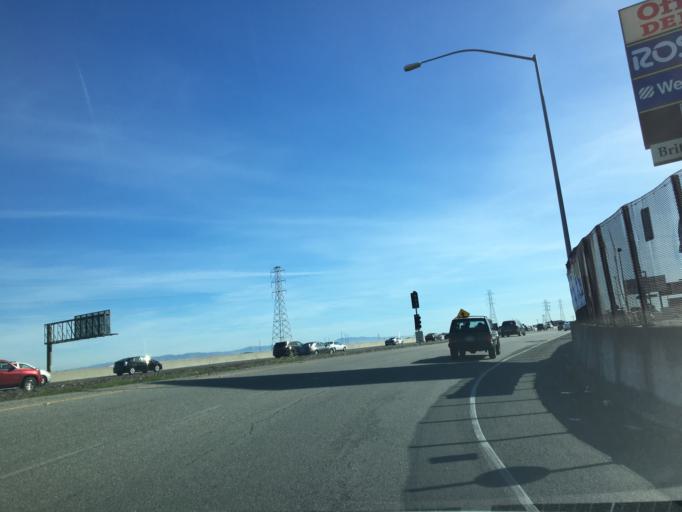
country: US
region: California
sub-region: San Mateo County
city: San Carlos
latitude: 37.5047
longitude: -122.2467
